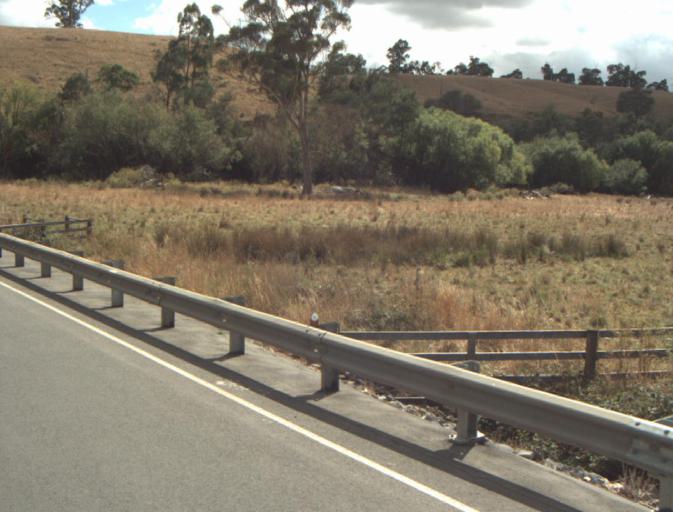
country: AU
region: Tasmania
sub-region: Launceston
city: Mayfield
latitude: -41.2208
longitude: 147.1373
